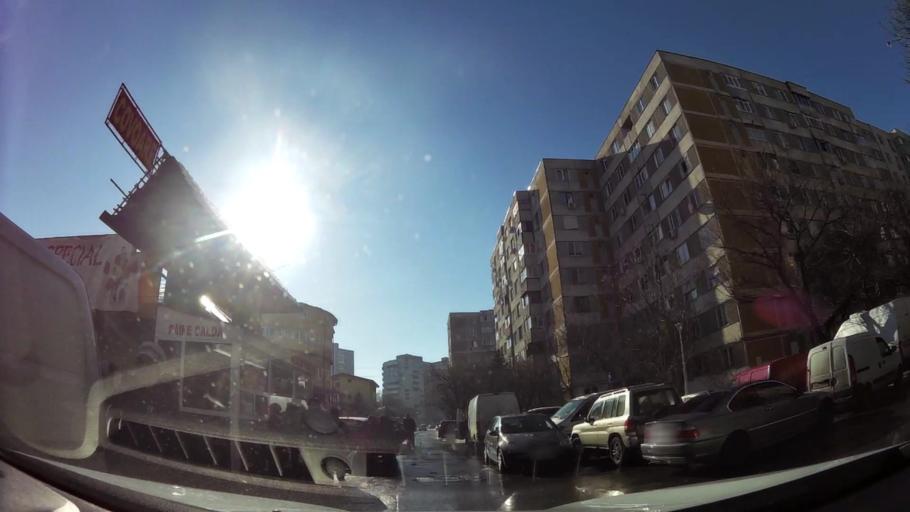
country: RO
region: Bucuresti
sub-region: Municipiul Bucuresti
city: Bucuresti
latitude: 44.4063
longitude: 26.0601
